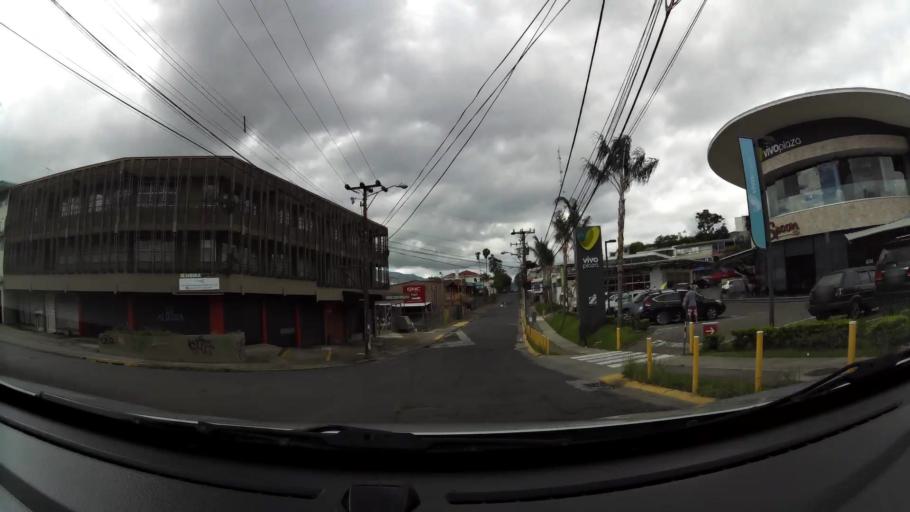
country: CR
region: San Jose
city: San Pedro
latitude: 9.9314
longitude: -84.0574
